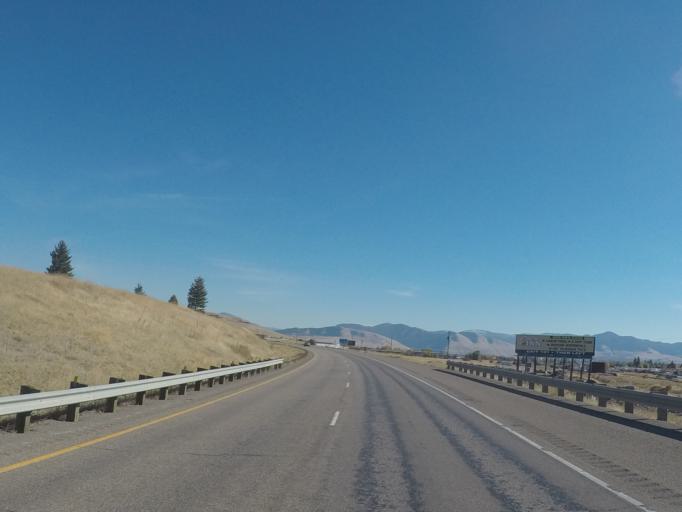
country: US
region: Montana
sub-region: Missoula County
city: Orchard Homes
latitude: 46.9397
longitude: -114.1110
